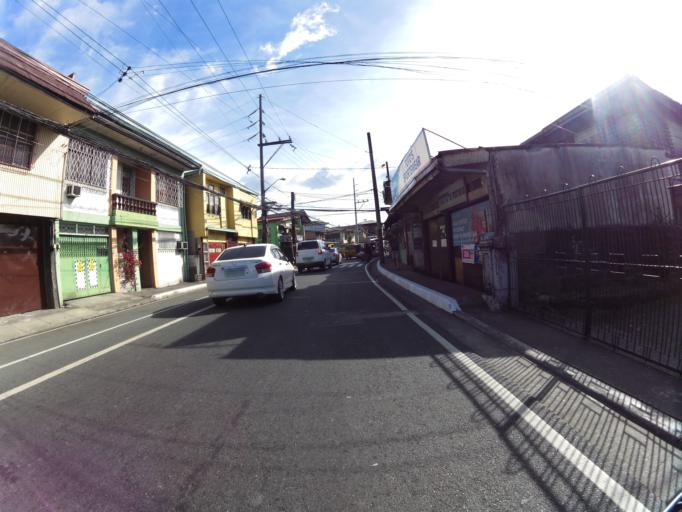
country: PH
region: Metro Manila
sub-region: Marikina
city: Calumpang
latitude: 14.6276
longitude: 121.0970
